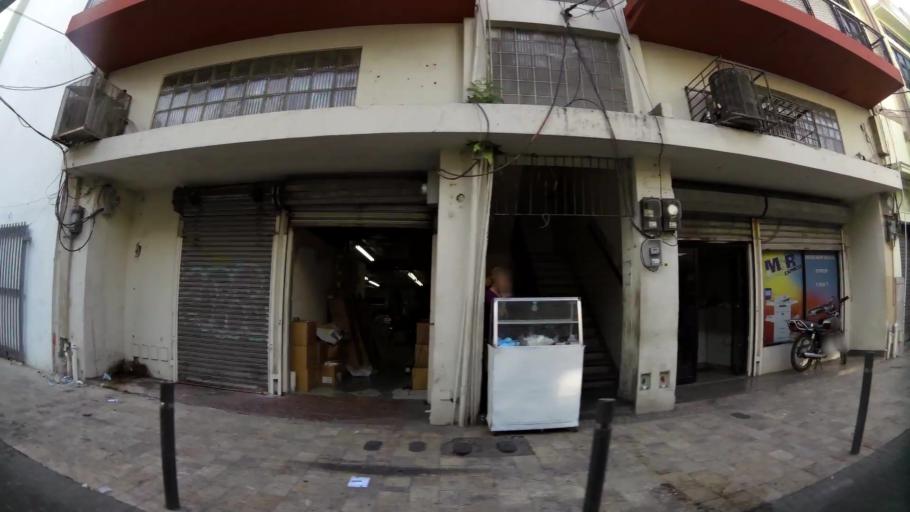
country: DO
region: Nacional
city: San Carlos
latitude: 18.4759
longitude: -69.8848
